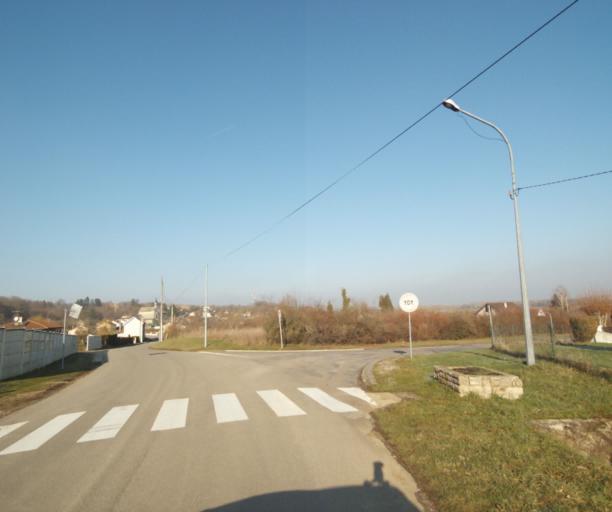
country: FR
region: Champagne-Ardenne
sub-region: Departement de la Haute-Marne
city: Wassy
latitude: 48.5103
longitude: 4.9202
